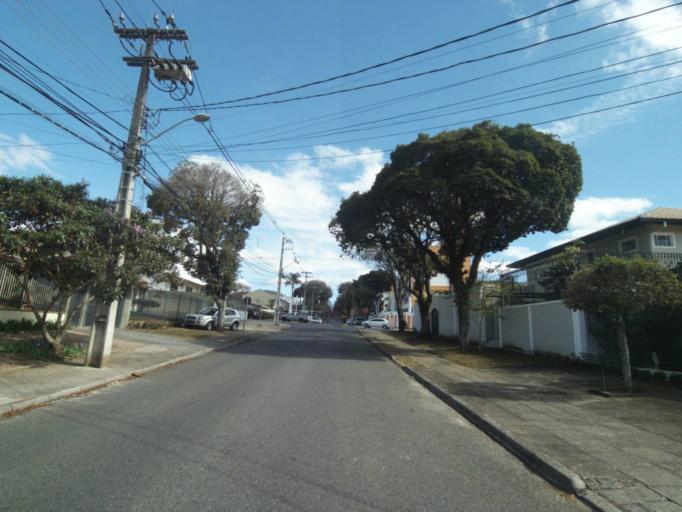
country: BR
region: Parana
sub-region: Curitiba
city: Curitiba
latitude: -25.4619
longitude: -49.2778
